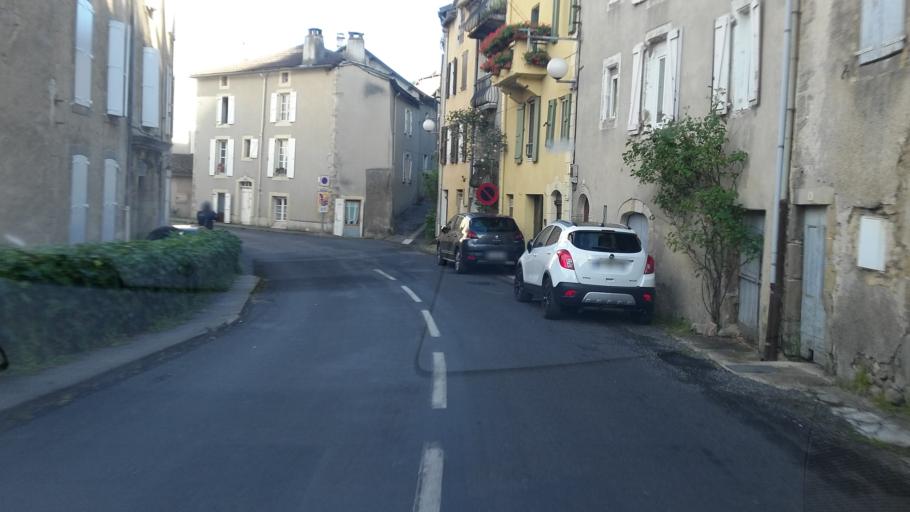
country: FR
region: Languedoc-Roussillon
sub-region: Departement de la Lozere
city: Meyrueis
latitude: 44.0236
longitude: 3.3581
